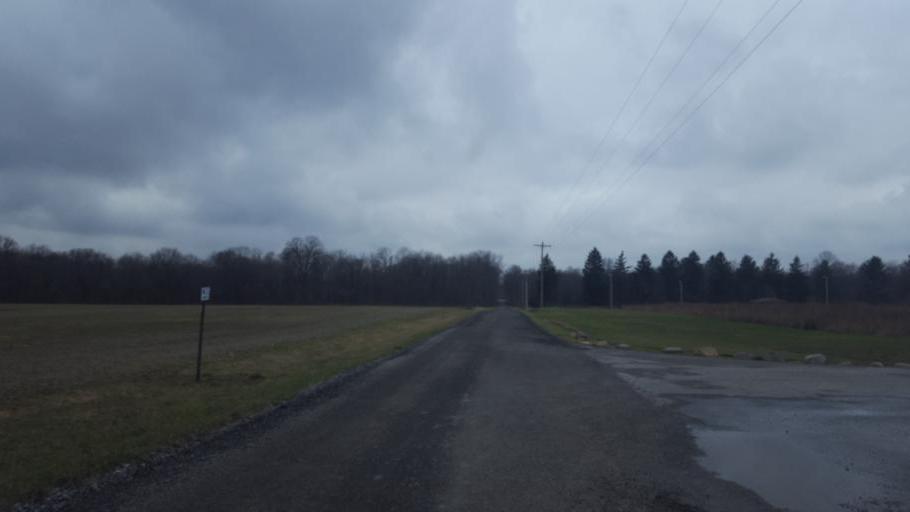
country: US
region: Ohio
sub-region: Delaware County
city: Ashley
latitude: 40.3735
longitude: -82.8714
